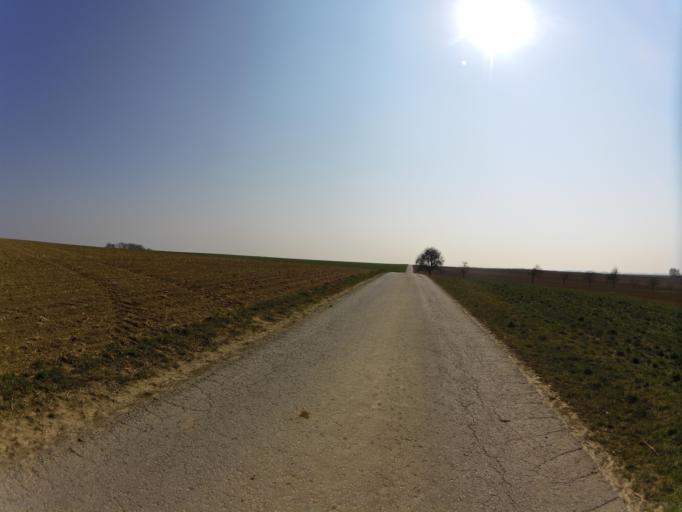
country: DE
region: Bavaria
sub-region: Regierungsbezirk Unterfranken
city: Eibelstadt
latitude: 49.6958
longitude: 9.9811
